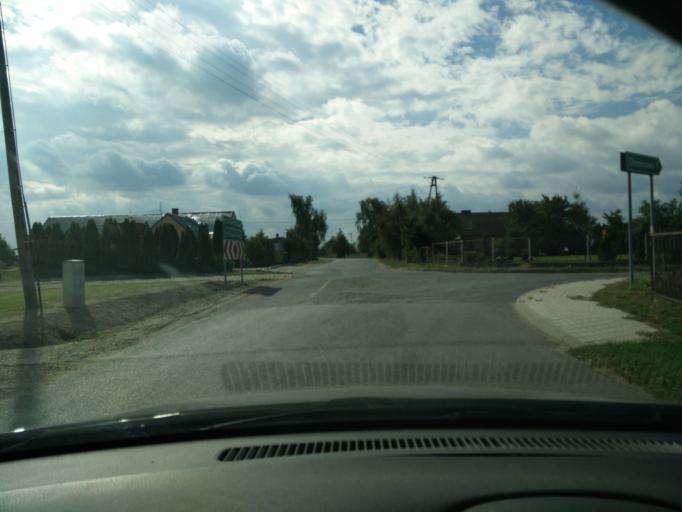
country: PL
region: Greater Poland Voivodeship
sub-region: Powiat sredzki
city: Dominowo
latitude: 52.2889
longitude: 17.3818
